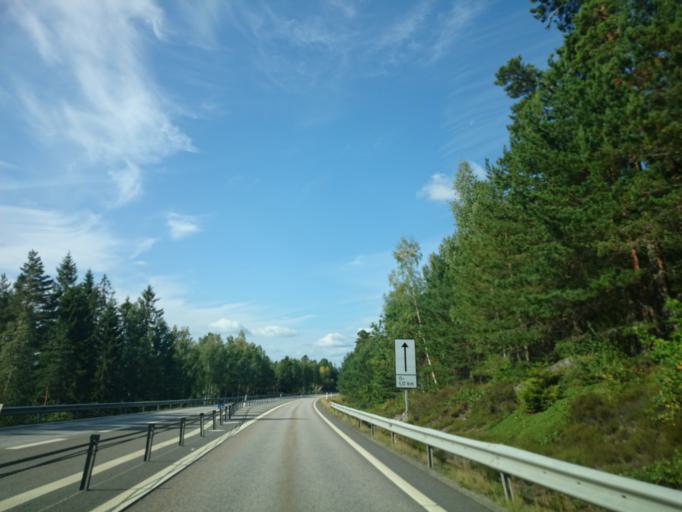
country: SE
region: OEstergoetland
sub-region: Valdemarsviks Kommun
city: Valdemarsvik
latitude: 58.0995
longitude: 16.5363
